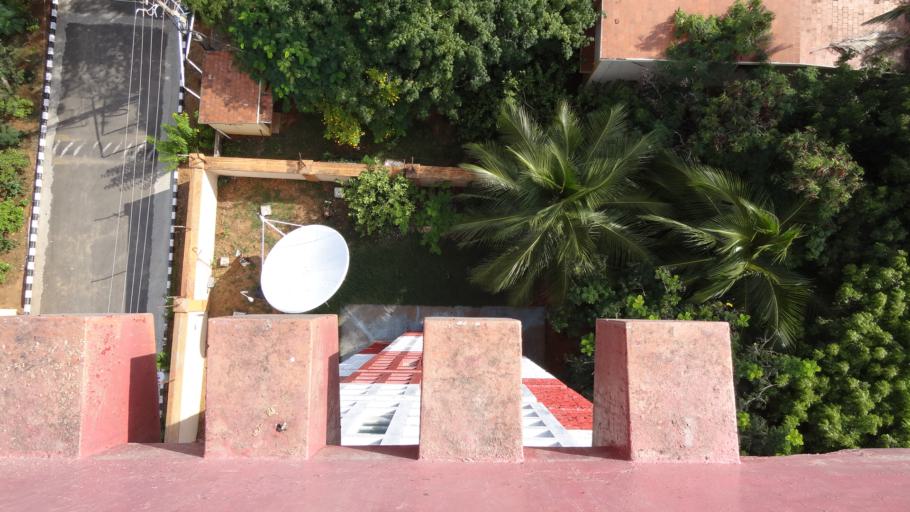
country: IN
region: Tamil Nadu
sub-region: Kanniyakumari
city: Kanniyakumari
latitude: 8.0821
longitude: 77.5467
